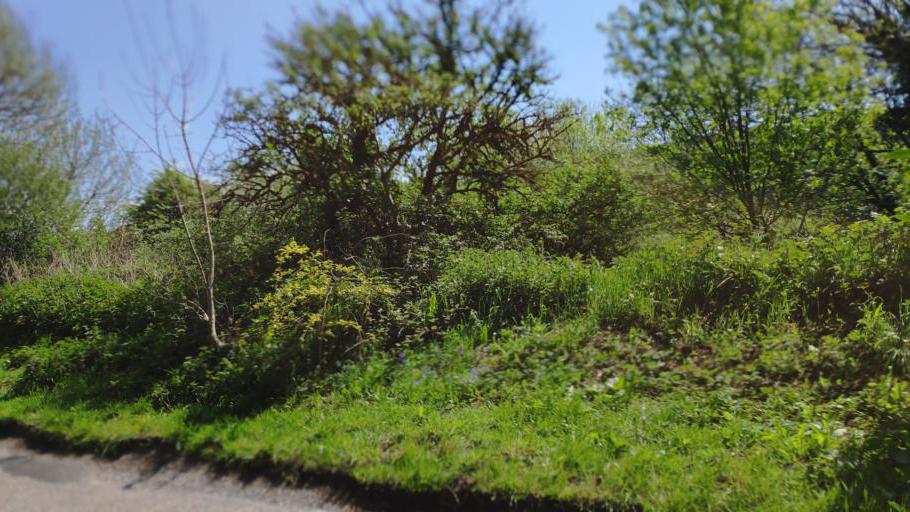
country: IE
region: Munster
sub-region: County Cork
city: Cork
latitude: 51.9152
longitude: -8.5179
